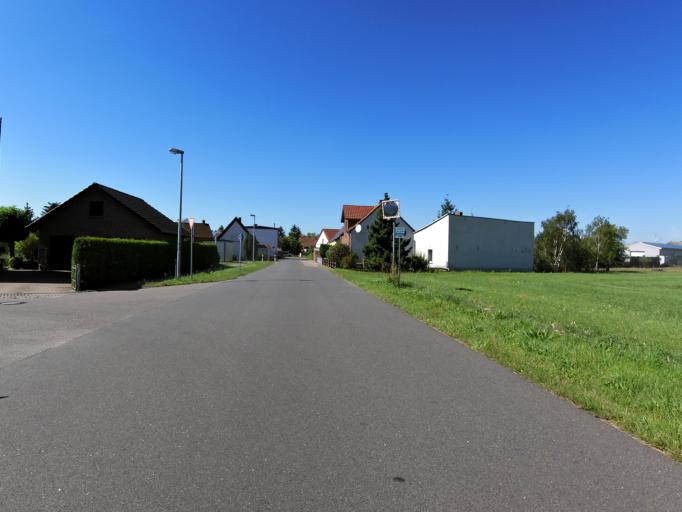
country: DE
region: Saxony-Anhalt
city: Muhlanger
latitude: 51.8450
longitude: 12.7459
